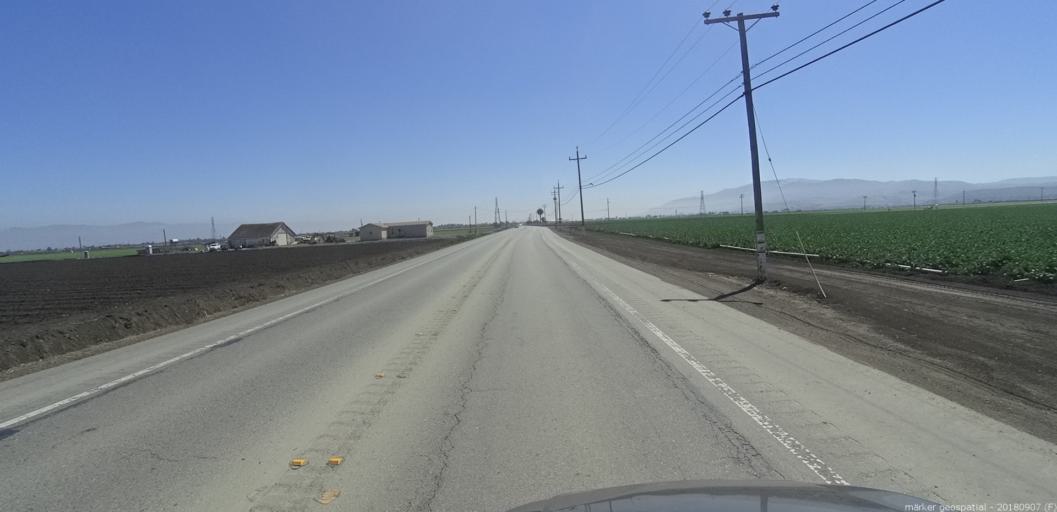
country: US
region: California
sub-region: Monterey County
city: Boronda
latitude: 36.6775
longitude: -121.7038
